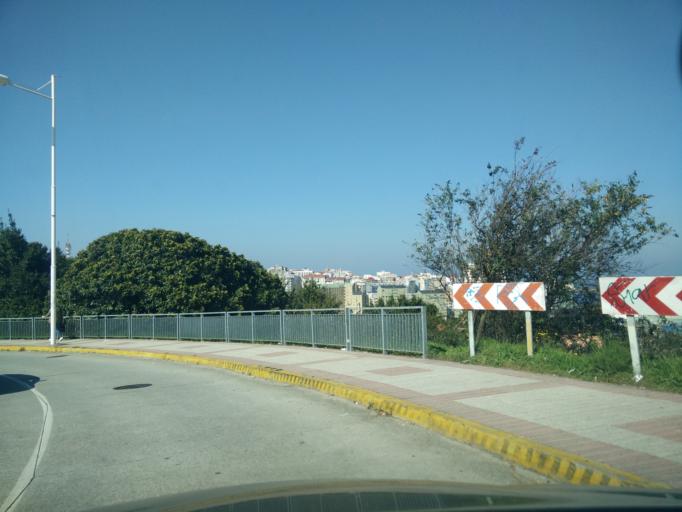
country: ES
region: Galicia
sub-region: Provincia da Coruna
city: A Coruna
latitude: 43.3456
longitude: -8.3890
